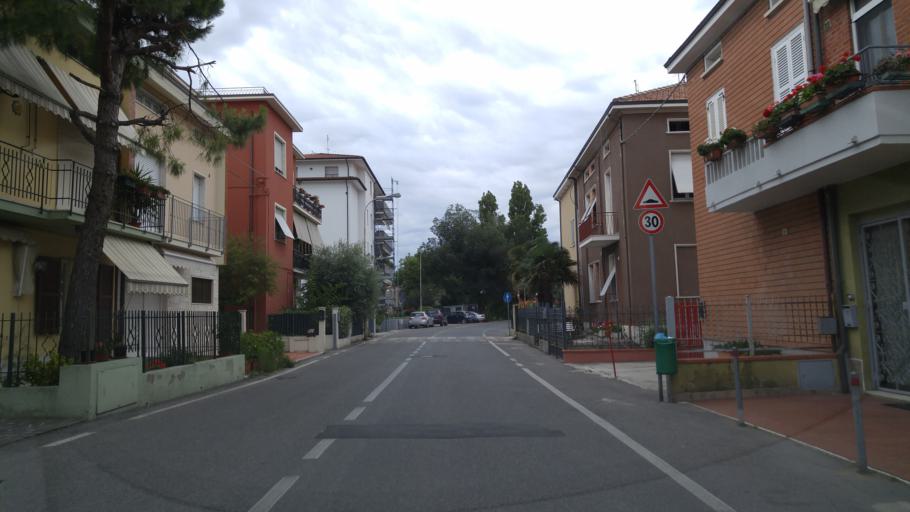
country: IT
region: The Marches
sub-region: Provincia di Pesaro e Urbino
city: Pesaro
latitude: 43.9136
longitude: 12.9016
